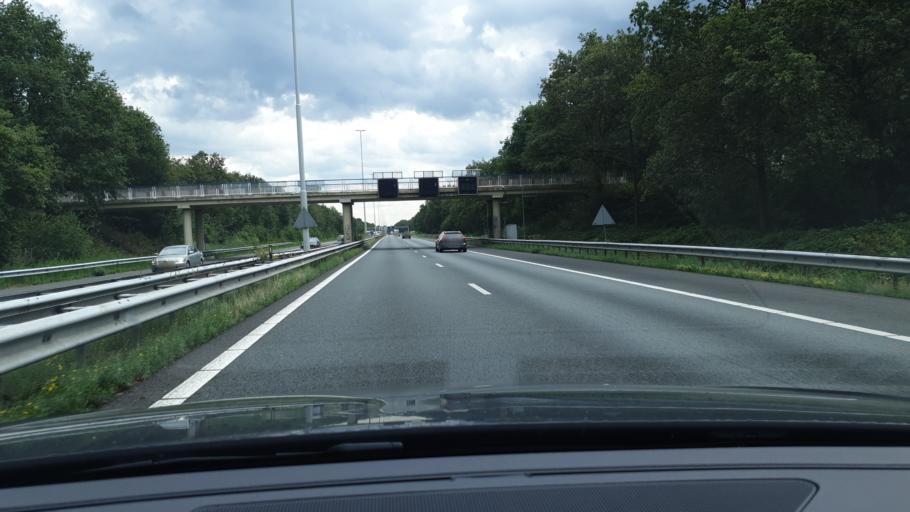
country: NL
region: North Brabant
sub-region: Gemeente Oirschot
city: Oostelbeers
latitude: 51.5088
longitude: 5.2721
